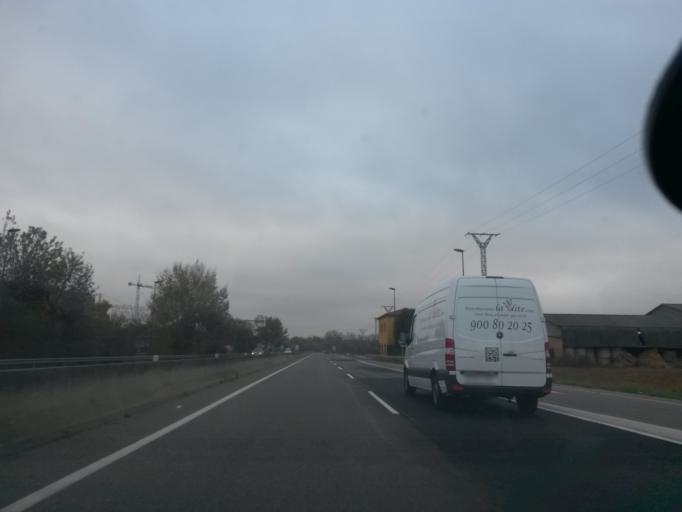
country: ES
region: Catalonia
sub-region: Provincia de Girona
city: Cornella del Terri
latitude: 42.0747
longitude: 2.8162
